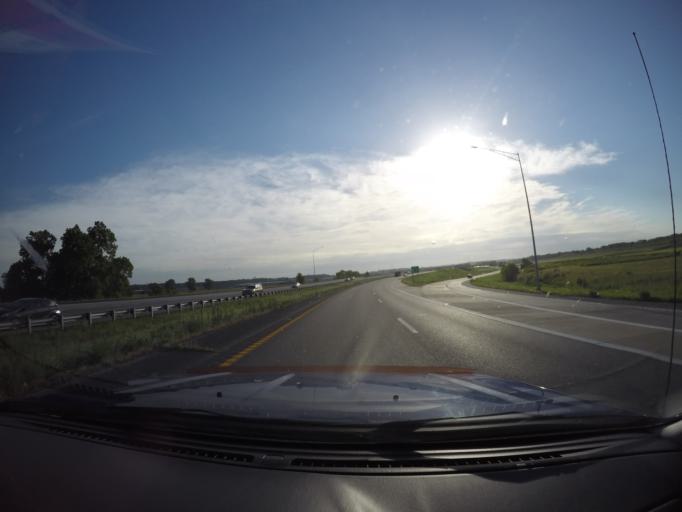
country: US
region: Missouri
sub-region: Platte County
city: Riverside
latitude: 39.1594
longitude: -94.6462
